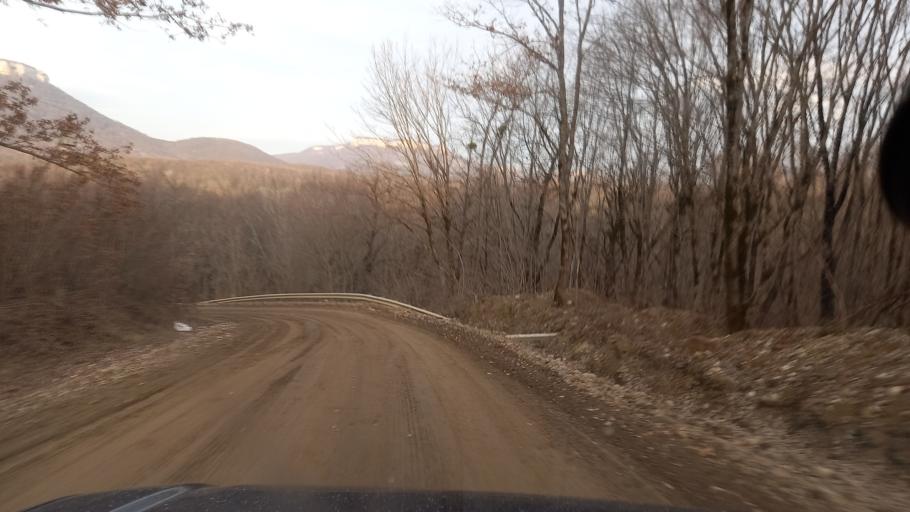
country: RU
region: Adygeya
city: Kamennomostskiy
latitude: 44.2090
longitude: 40.2543
